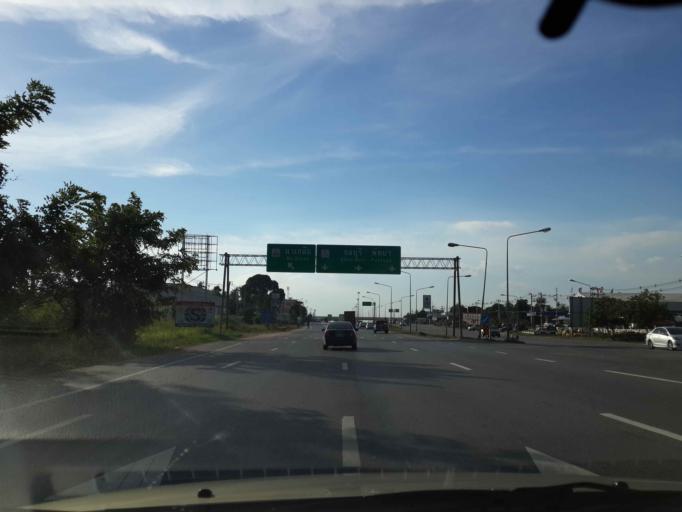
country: TH
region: Chon Buri
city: Phatthaya
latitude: 12.9476
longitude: 100.9910
